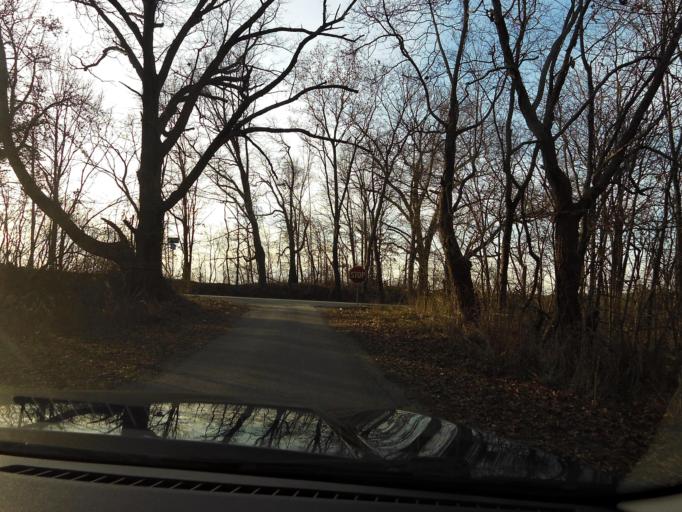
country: US
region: Illinois
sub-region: Fayette County
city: Vandalia
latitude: 38.9212
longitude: -89.2169
